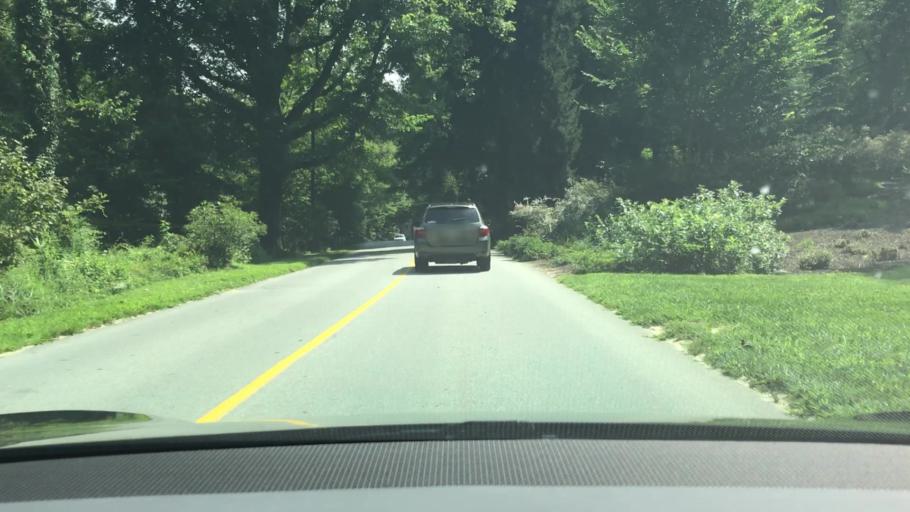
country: US
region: North Carolina
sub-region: Buncombe County
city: Asheville
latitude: 35.5654
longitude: -82.5487
